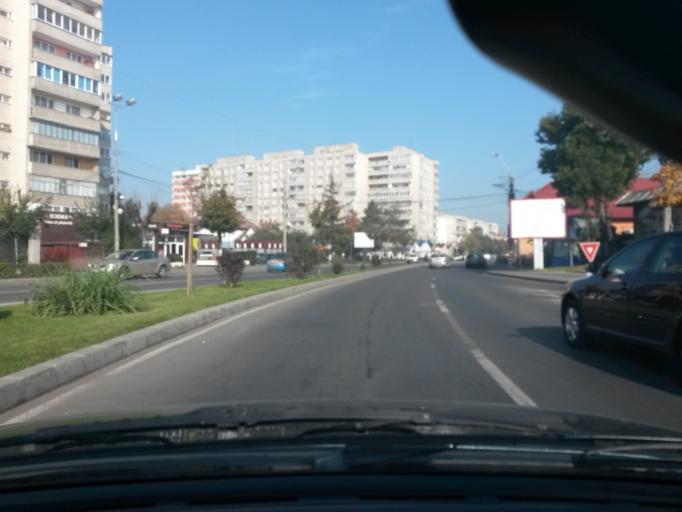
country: RO
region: Mures
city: Targu-Mures
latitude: 46.5317
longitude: 24.5505
